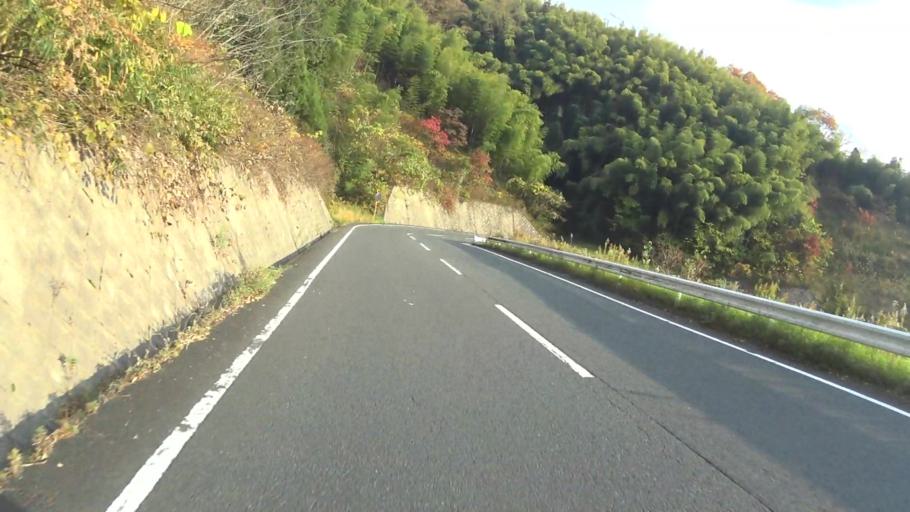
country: JP
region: Kyoto
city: Maizuru
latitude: 35.5155
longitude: 135.4579
